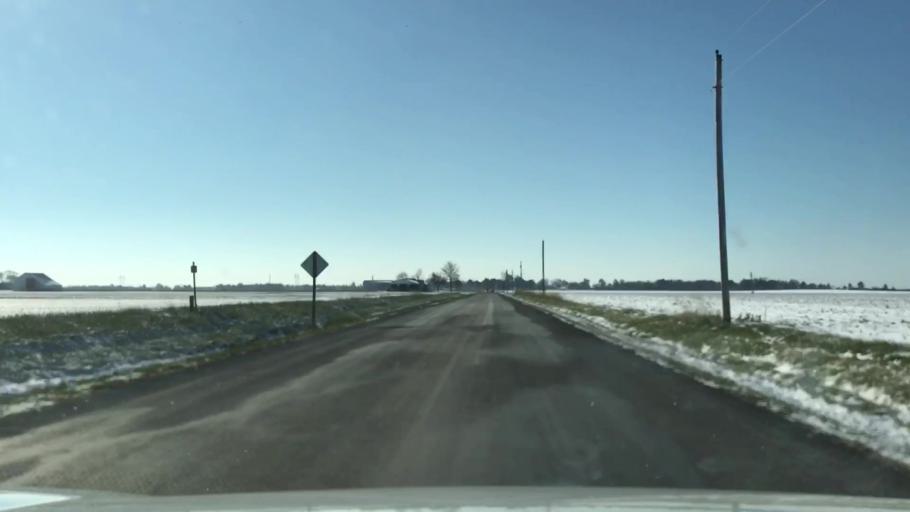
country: US
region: Illinois
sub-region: Washington County
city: Okawville
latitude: 38.4095
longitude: -89.4867
